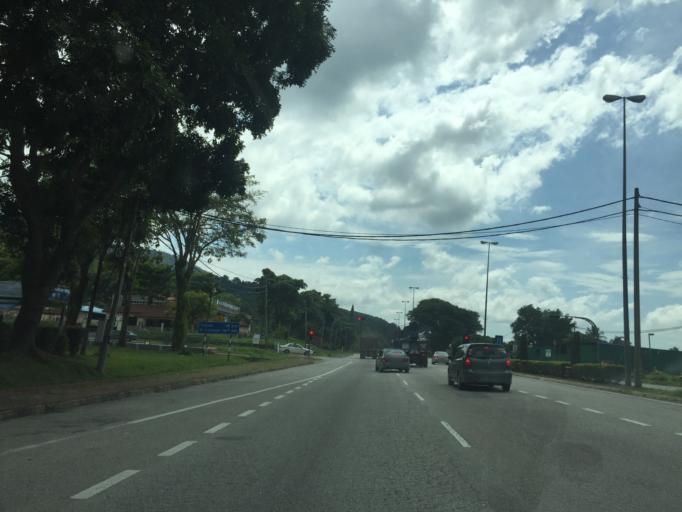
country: MY
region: Perak
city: Kampar
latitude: 4.2994
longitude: 101.1598
